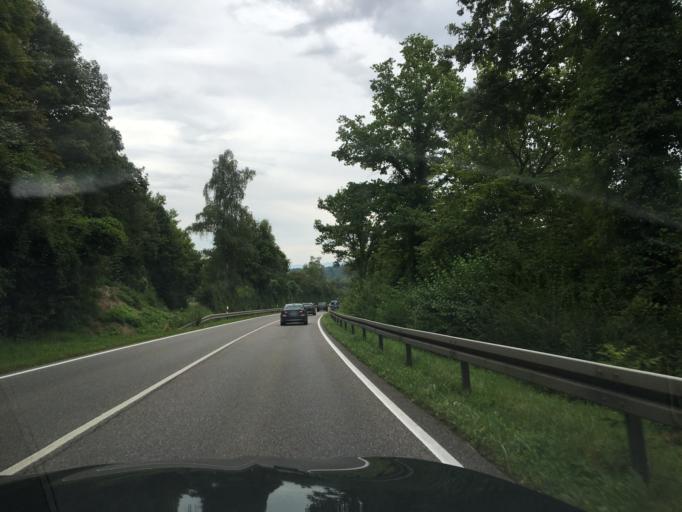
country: DE
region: Baden-Wuerttemberg
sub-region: Freiburg Region
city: Radolfzell am Bodensee
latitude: 47.7753
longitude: 8.9819
